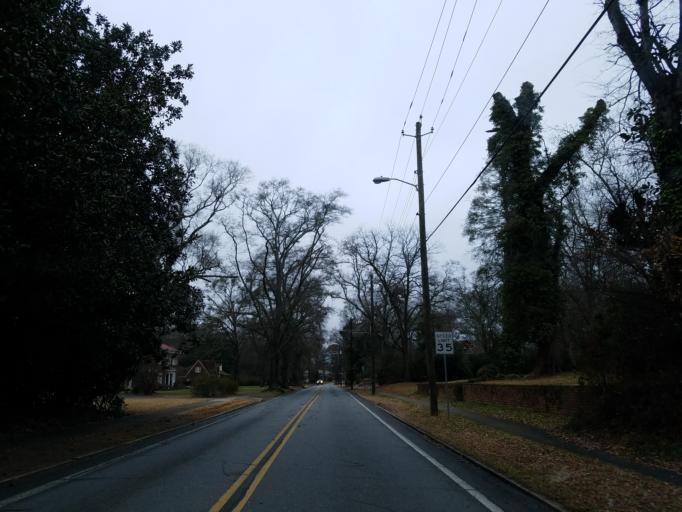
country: US
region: Georgia
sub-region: Bartow County
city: Cartersville
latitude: 34.1656
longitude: -84.8040
